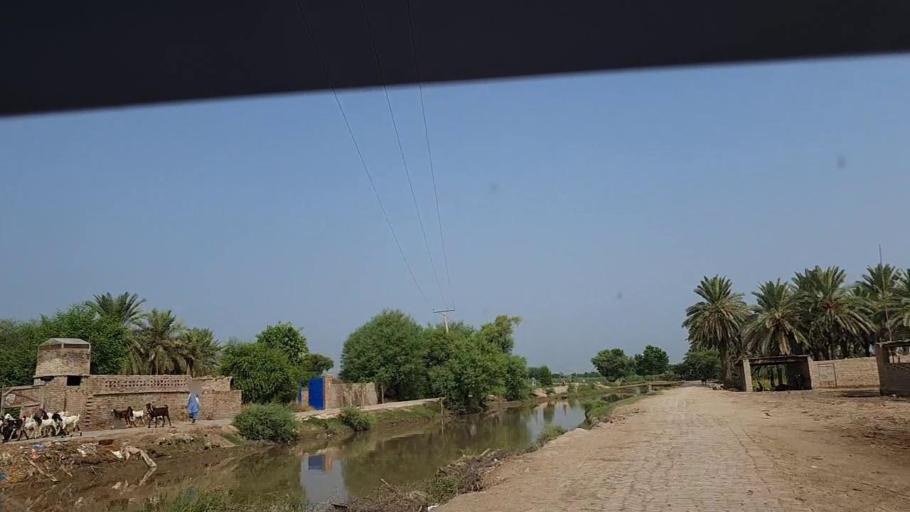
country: PK
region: Sindh
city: Adilpur
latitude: 27.9663
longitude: 69.3171
